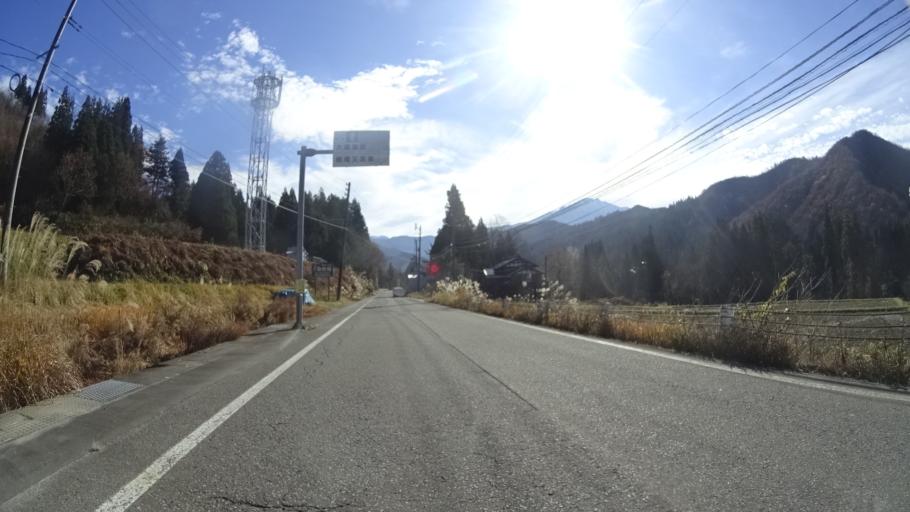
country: JP
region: Niigata
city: Muikamachi
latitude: 37.2014
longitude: 139.0754
